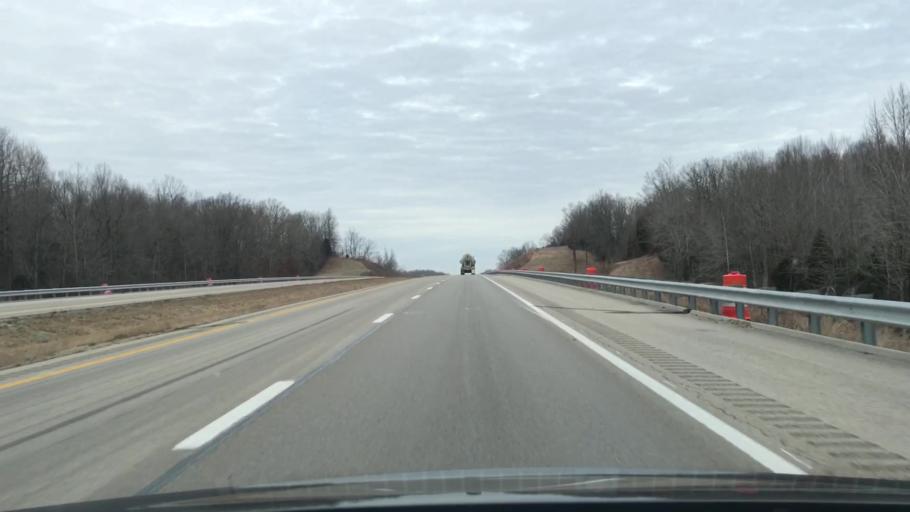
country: US
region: Kentucky
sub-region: Ohio County
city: Hartford
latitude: 37.5651
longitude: -86.9460
